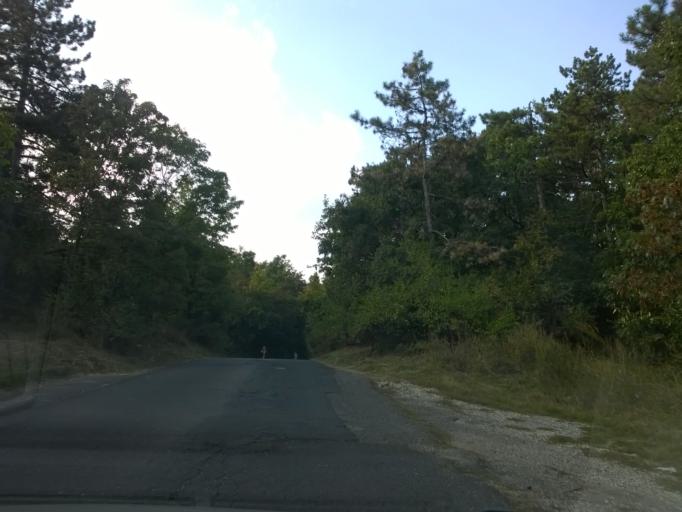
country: HU
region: Budapest
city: Budapest III. keruelet
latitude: 47.5516
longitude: 19.0034
